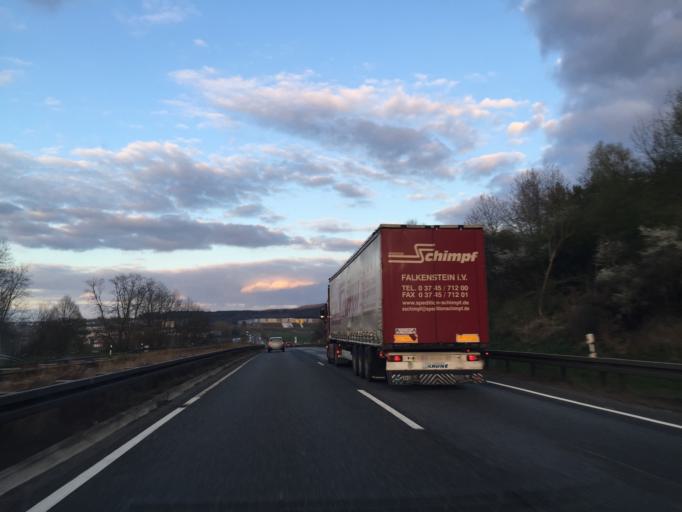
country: DE
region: Hesse
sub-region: Regierungsbezirk Kassel
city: Bad Hersfeld
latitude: 50.8532
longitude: 9.7092
